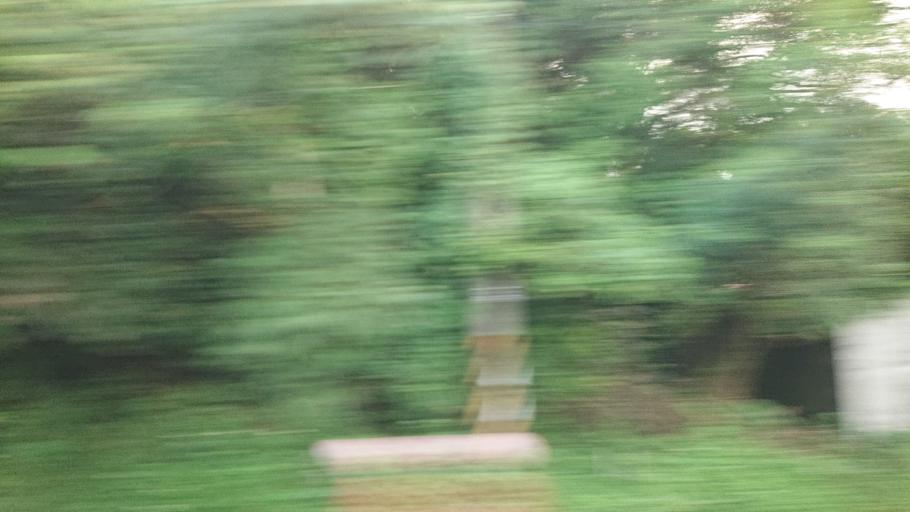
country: TW
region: Taiwan
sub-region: Nantou
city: Puli
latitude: 23.9715
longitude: 120.9961
